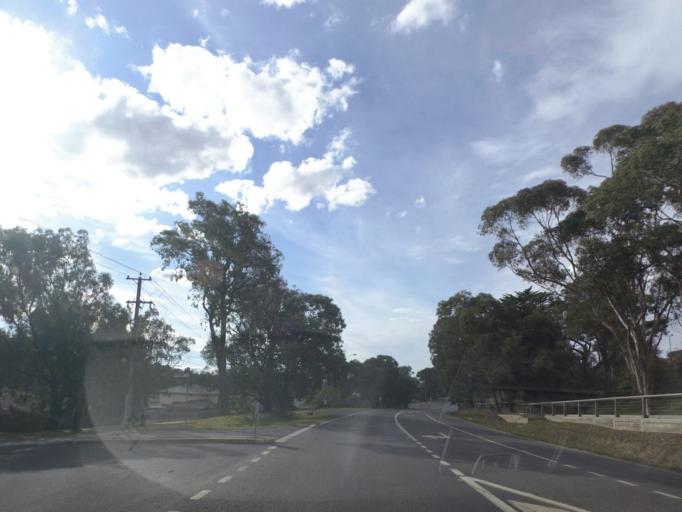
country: AU
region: Victoria
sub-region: Manningham
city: Donvale
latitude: -37.7575
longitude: 145.1735
